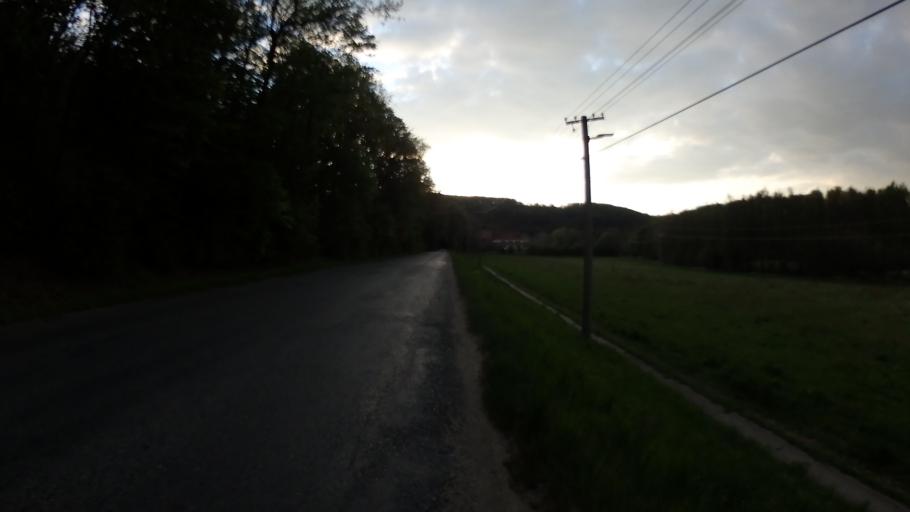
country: CZ
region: South Moravian
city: Strelice
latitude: 49.1373
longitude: 16.4716
